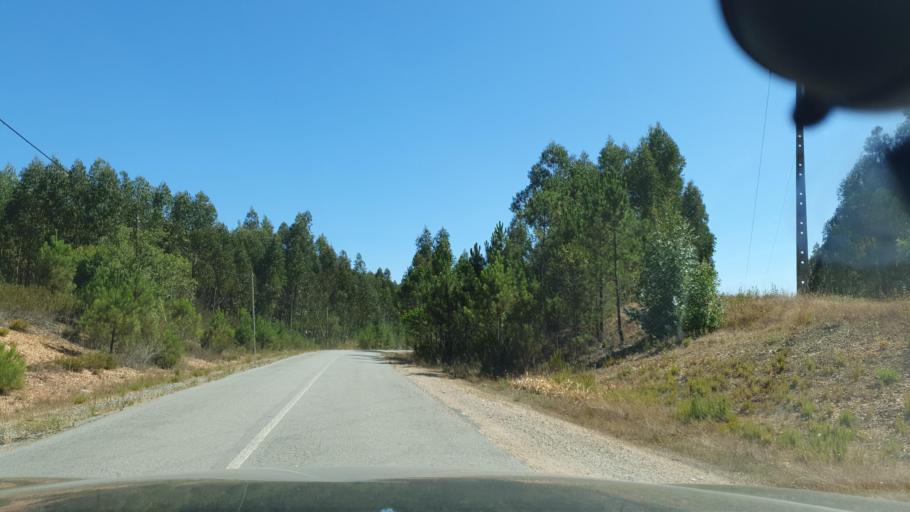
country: PT
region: Beja
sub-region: Odemira
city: Sao Teotonio
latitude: 37.4987
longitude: -8.6641
